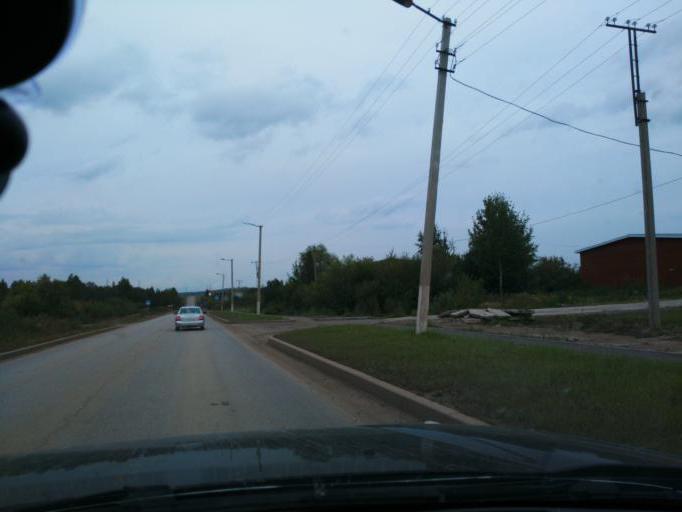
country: RU
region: Perm
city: Chernushka
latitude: 56.5388
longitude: 56.0995
